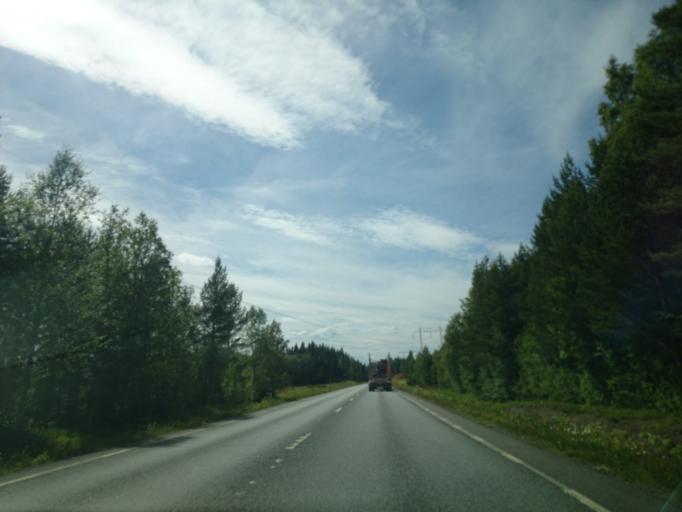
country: SE
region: Jaemtland
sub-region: Krokoms Kommun
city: Krokom
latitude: 63.3214
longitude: 14.2409
